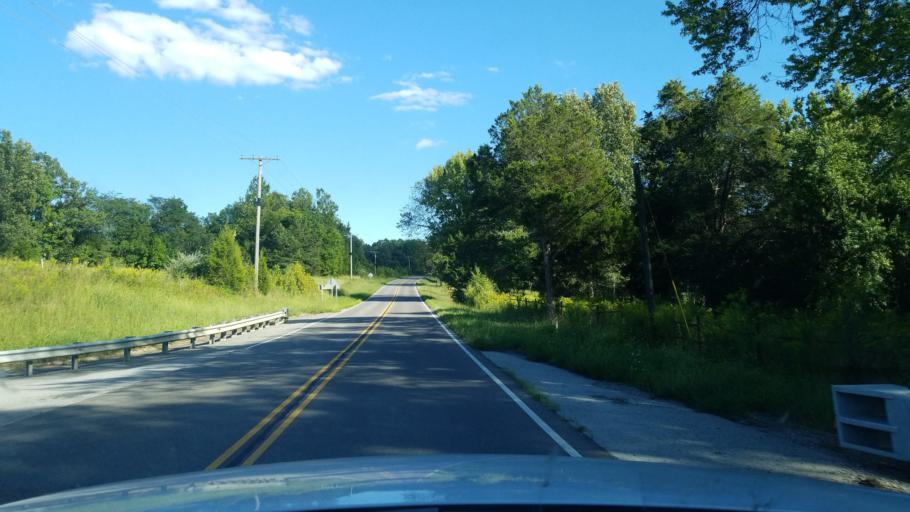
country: US
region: Illinois
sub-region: Saline County
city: Harrisburg
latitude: 37.6357
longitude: -88.4836
